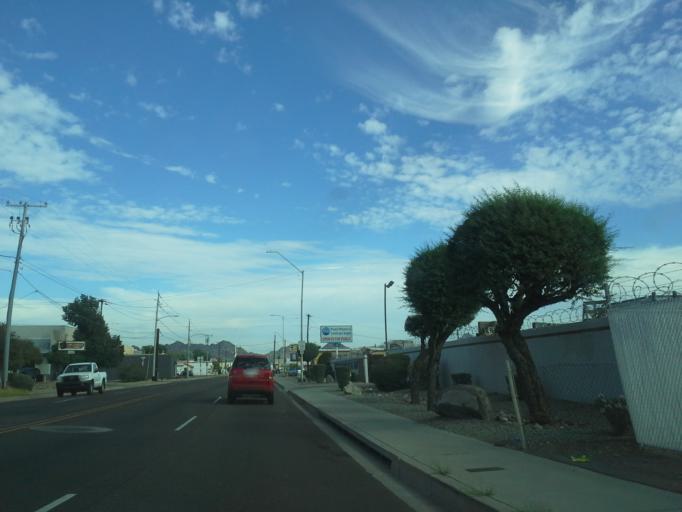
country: US
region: Arizona
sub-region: Maricopa County
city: Glendale
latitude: 33.5712
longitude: -112.0947
